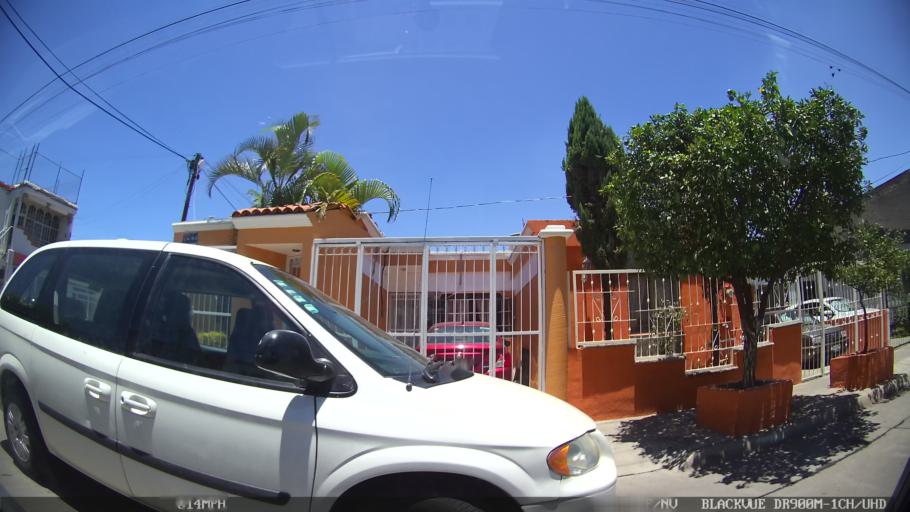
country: MX
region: Jalisco
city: Tlaquepaque
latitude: 20.6693
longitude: -103.2931
